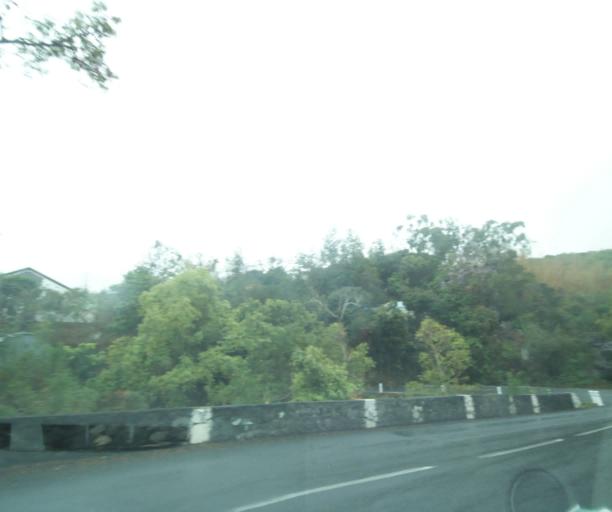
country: RE
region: Reunion
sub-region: Reunion
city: Saint-Paul
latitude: -21.0221
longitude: 55.2942
